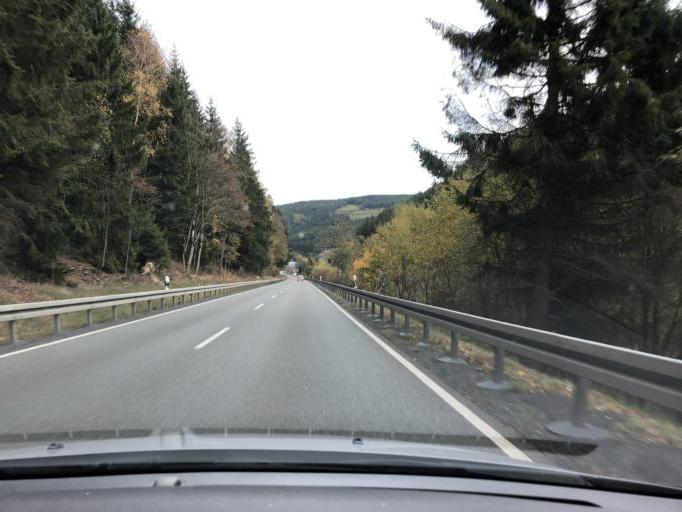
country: DE
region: Thuringia
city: Lichte
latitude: 50.5205
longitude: 11.1627
